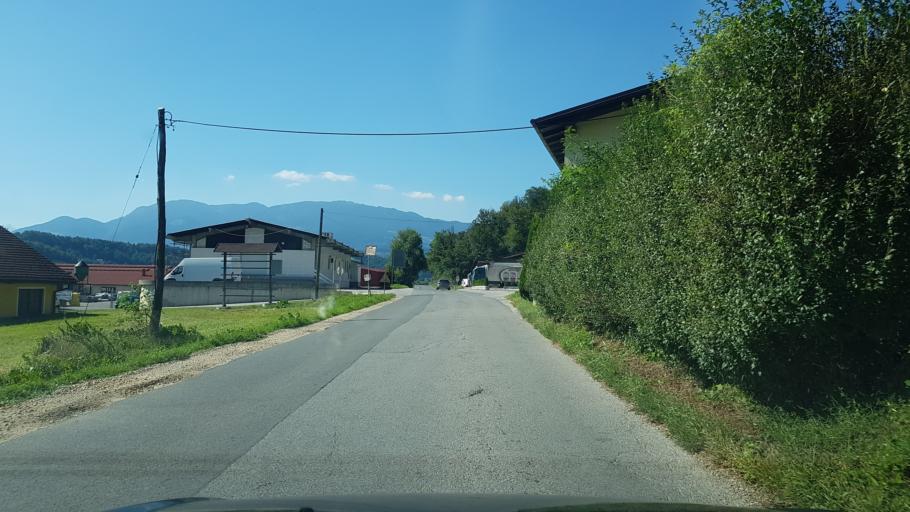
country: SI
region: Smartno ob Paki
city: Smartno ob Paki
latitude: 46.3332
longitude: 15.0336
